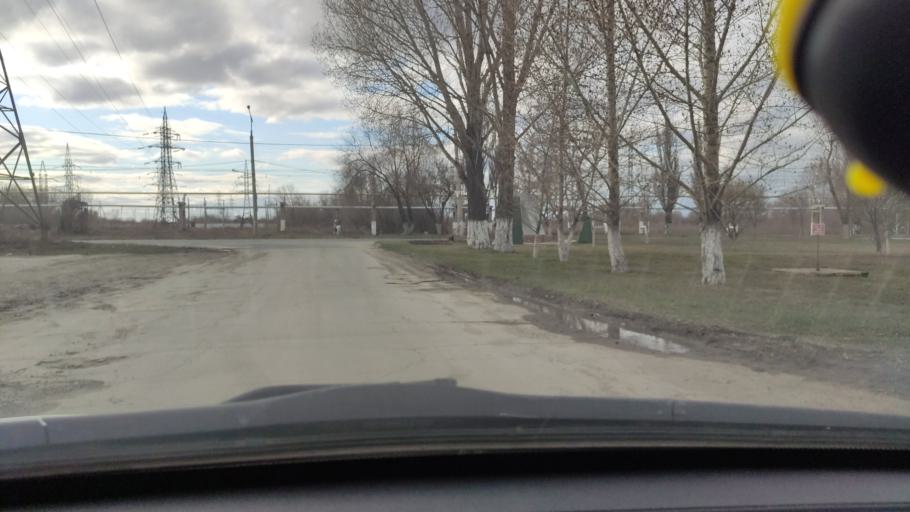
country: RU
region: Samara
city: Tol'yatti
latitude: 53.5511
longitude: 49.4500
